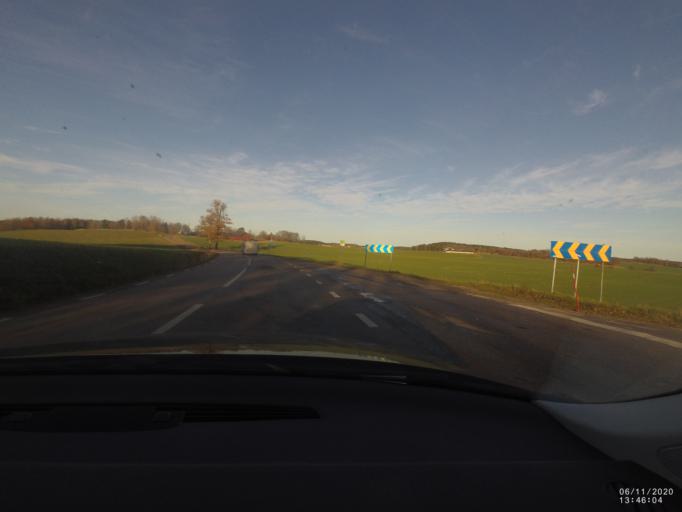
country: SE
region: Soedermanland
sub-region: Nykopings Kommun
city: Nykoping
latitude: 58.8833
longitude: 17.0895
